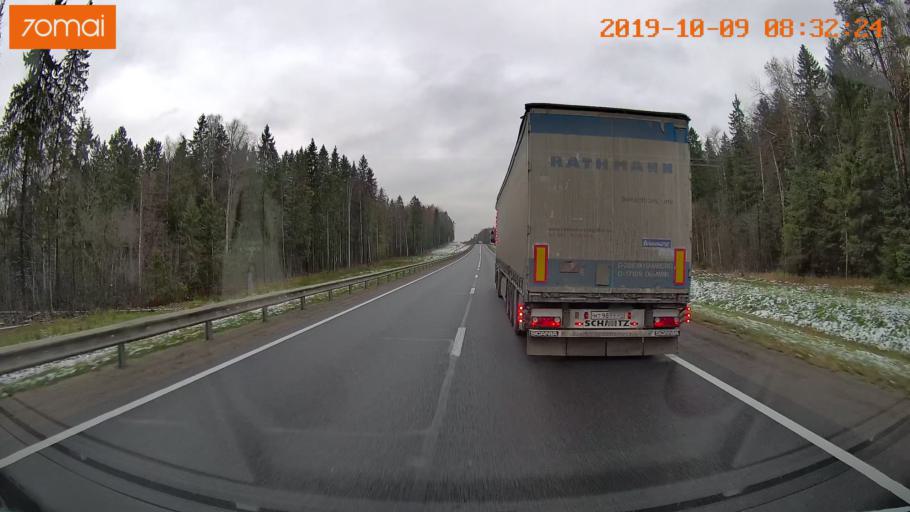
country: RU
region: Vologda
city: Gryazovets
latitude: 58.8661
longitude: 40.1978
